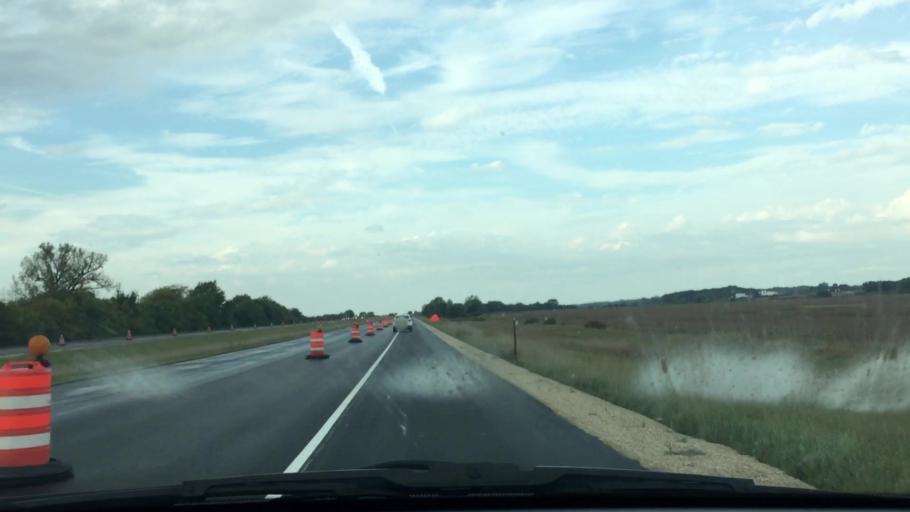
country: US
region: Illinois
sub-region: Whiteside County
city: Prophetstown
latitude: 41.7131
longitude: -90.0125
